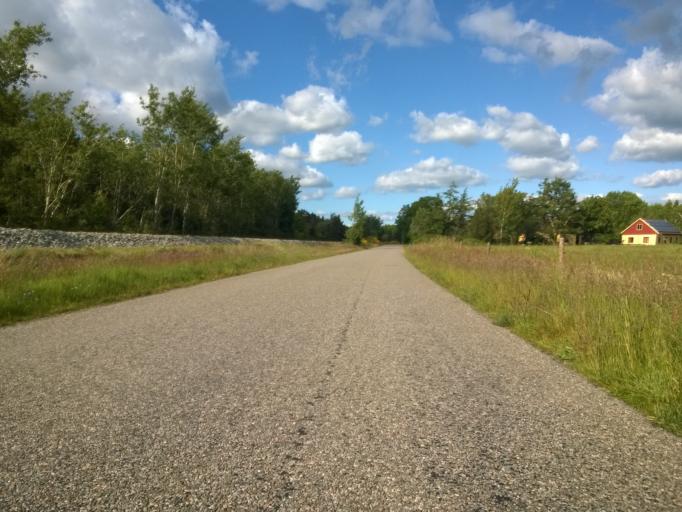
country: DK
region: Central Jutland
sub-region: Holstebro Kommune
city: Vinderup
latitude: 56.5107
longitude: 8.8496
